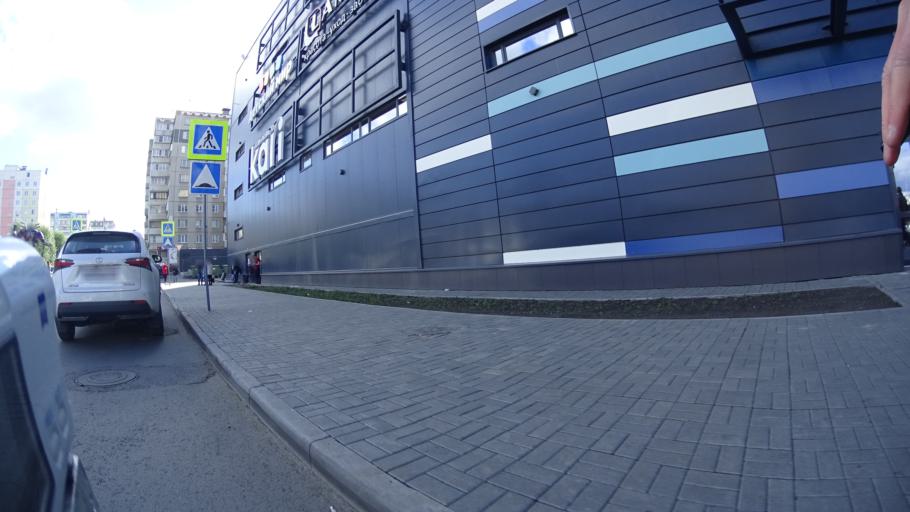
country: RU
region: Chelyabinsk
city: Roshchino
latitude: 55.1803
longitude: 61.2941
